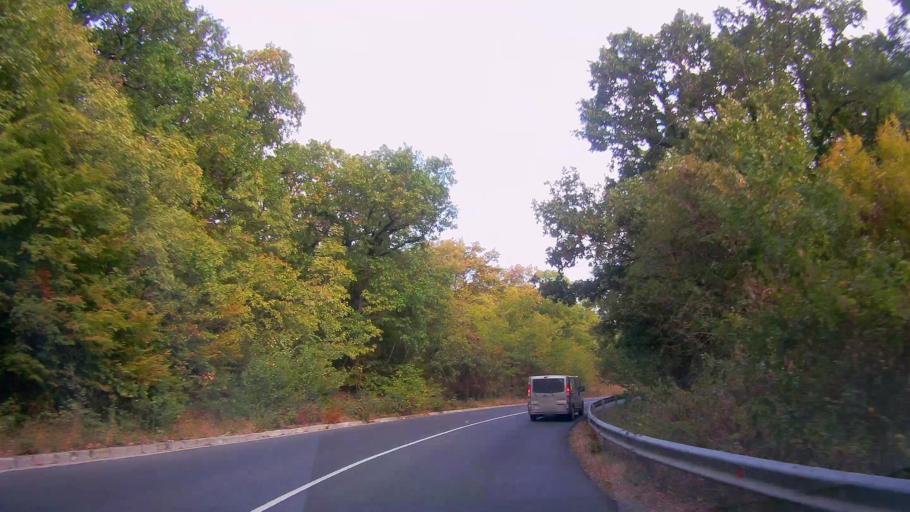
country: BG
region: Burgas
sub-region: Obshtina Primorsko
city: Primorsko
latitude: 42.3209
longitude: 27.7305
